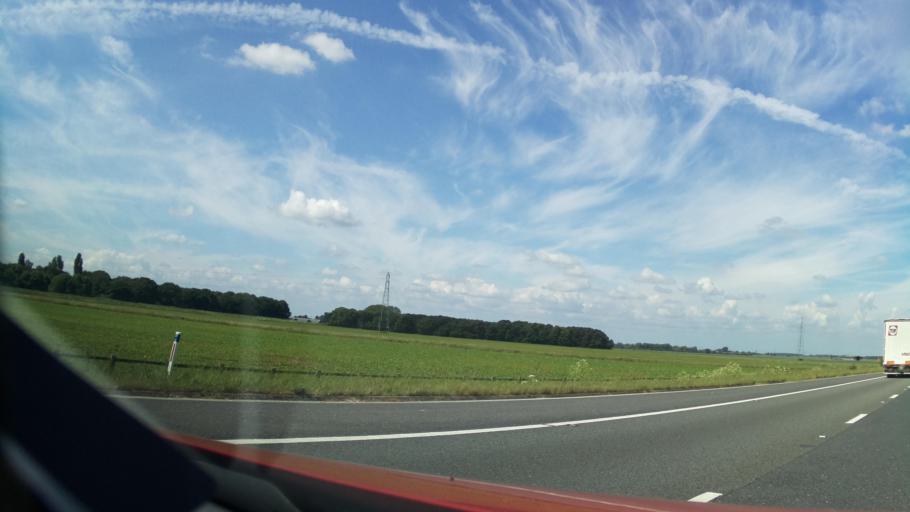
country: GB
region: England
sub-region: North Lincolnshire
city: Bottesford
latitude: 53.5454
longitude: -0.6832
